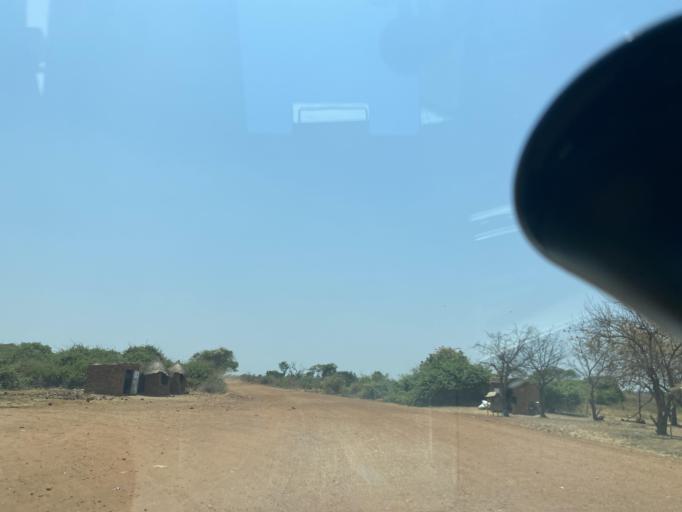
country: ZM
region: Southern
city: Nakambala
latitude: -15.4721
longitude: 27.9007
